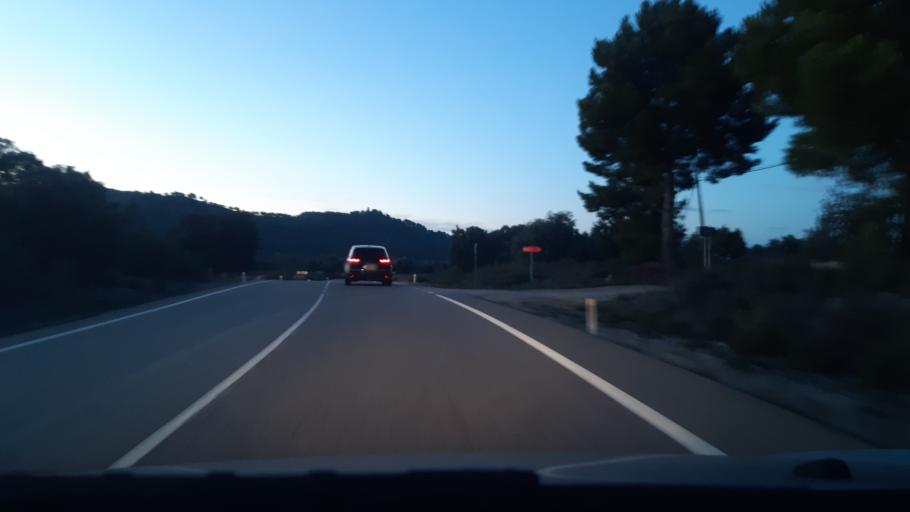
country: ES
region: Aragon
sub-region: Provincia de Teruel
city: Calaceite
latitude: 41.0004
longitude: 0.1946
